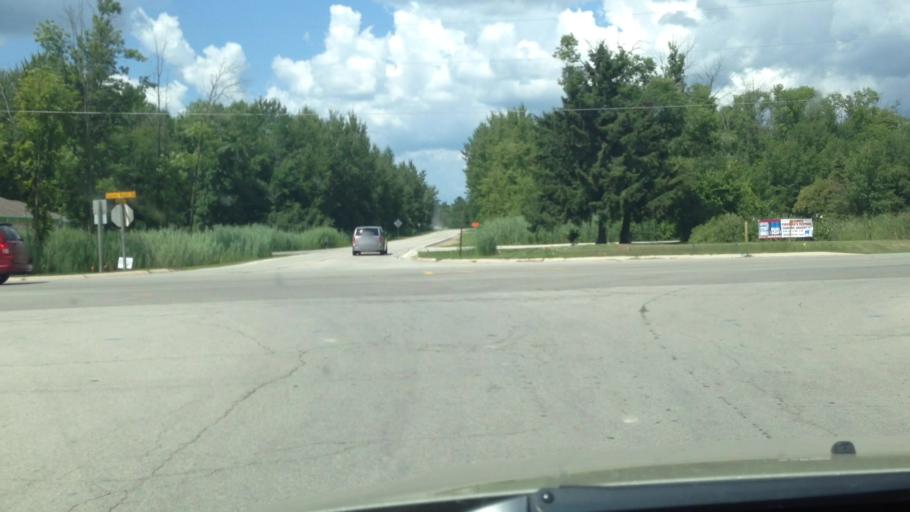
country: US
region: Wisconsin
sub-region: Brown County
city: Suamico
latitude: 44.6355
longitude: -88.0433
